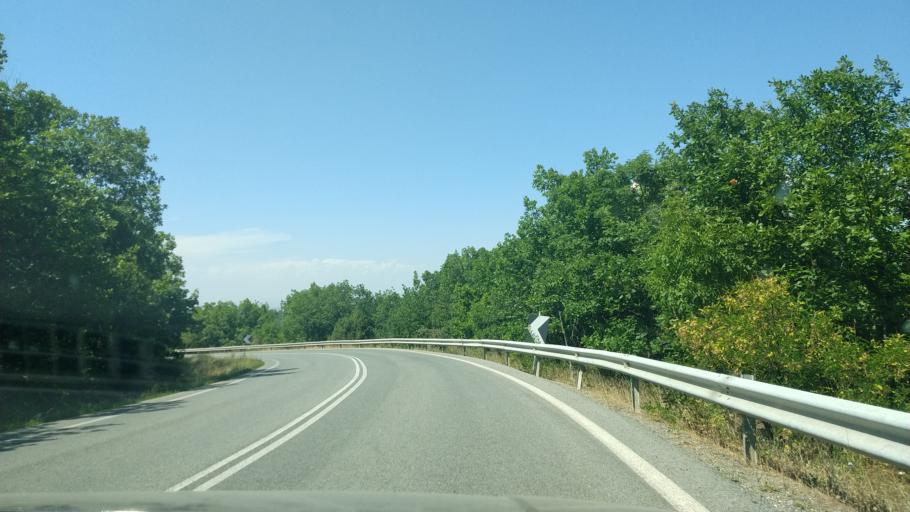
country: GR
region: West Macedonia
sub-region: Nomos Grevenon
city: Grevena
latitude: 39.9792
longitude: 21.5150
